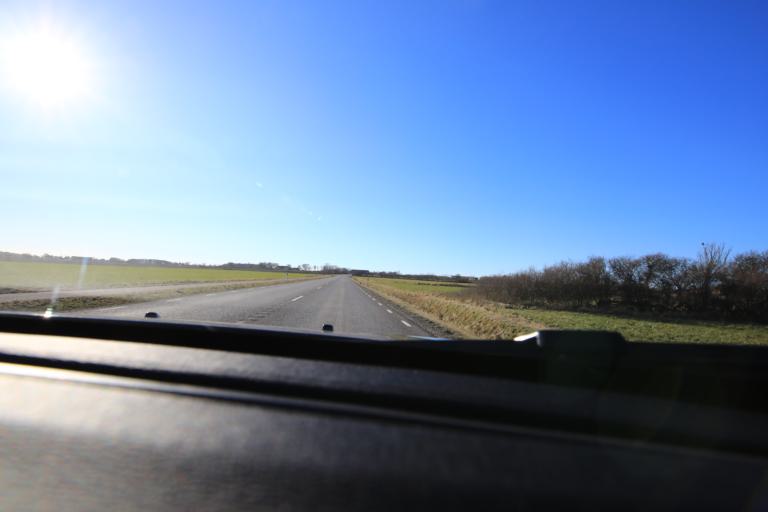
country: SE
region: Halland
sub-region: Varbergs Kommun
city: Tvaaker
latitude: 57.0484
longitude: 12.3416
